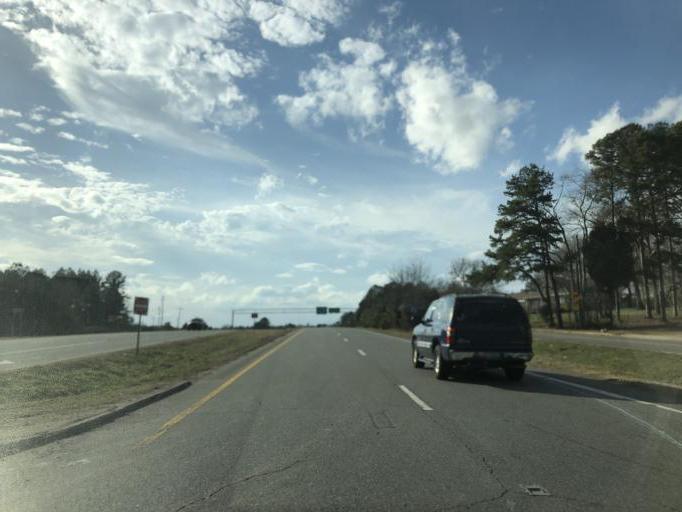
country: US
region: North Carolina
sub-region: Gaston County
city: Bessemer City
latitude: 35.2488
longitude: -81.2920
